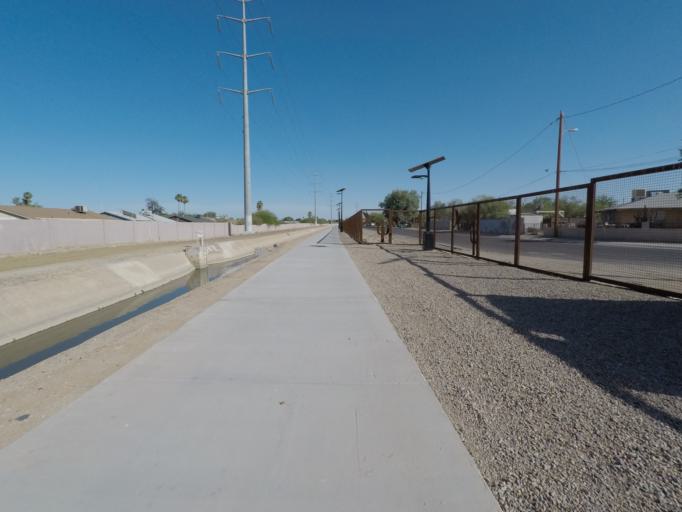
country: US
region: Arizona
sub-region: Maricopa County
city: Guadalupe
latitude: 33.3711
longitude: -111.9592
